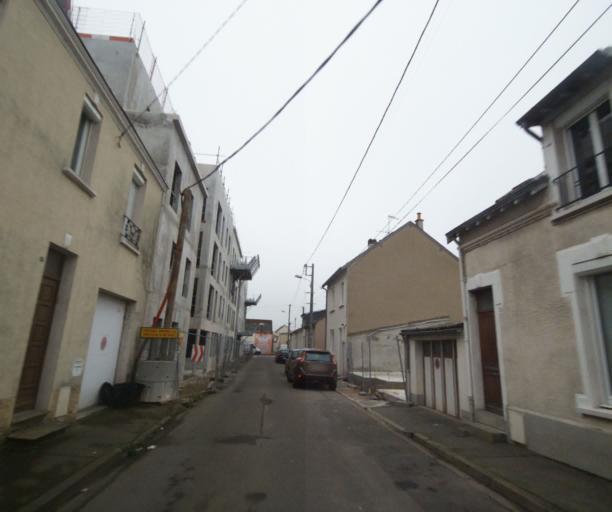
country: FR
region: Pays de la Loire
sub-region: Departement de la Sarthe
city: Le Mans
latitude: 47.9861
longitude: 0.2067
